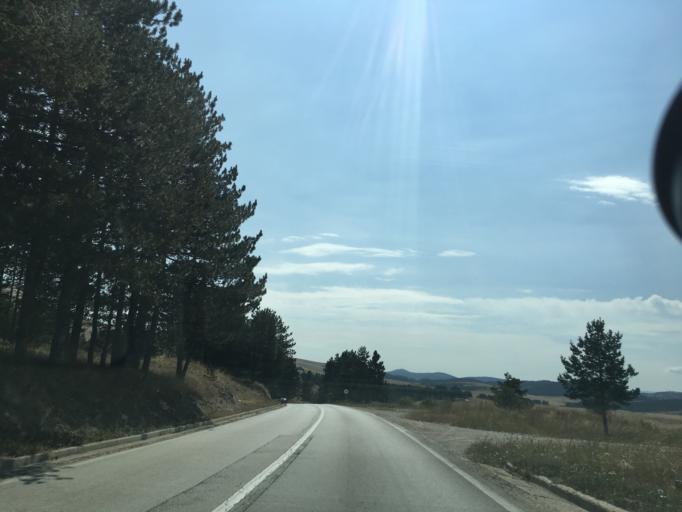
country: RS
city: Zlatibor
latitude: 43.6904
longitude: 19.6953
